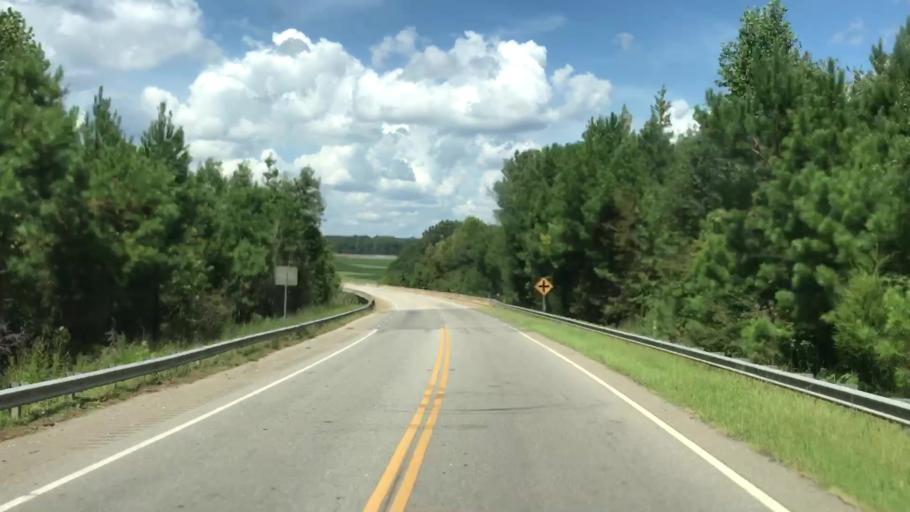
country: US
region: Georgia
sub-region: Greene County
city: Greensboro
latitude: 33.7194
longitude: -83.2939
